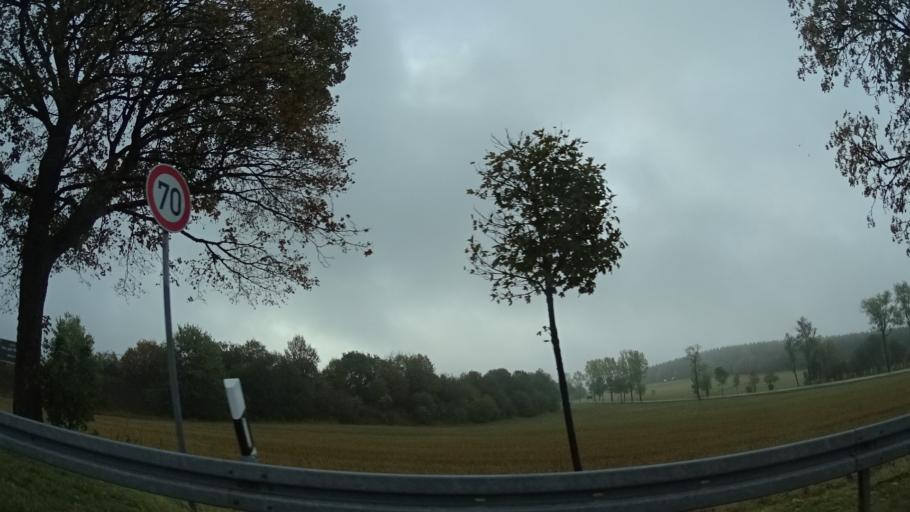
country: DE
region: Hesse
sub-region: Regierungsbezirk Giessen
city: Grebenhain
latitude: 50.4658
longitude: 9.2717
